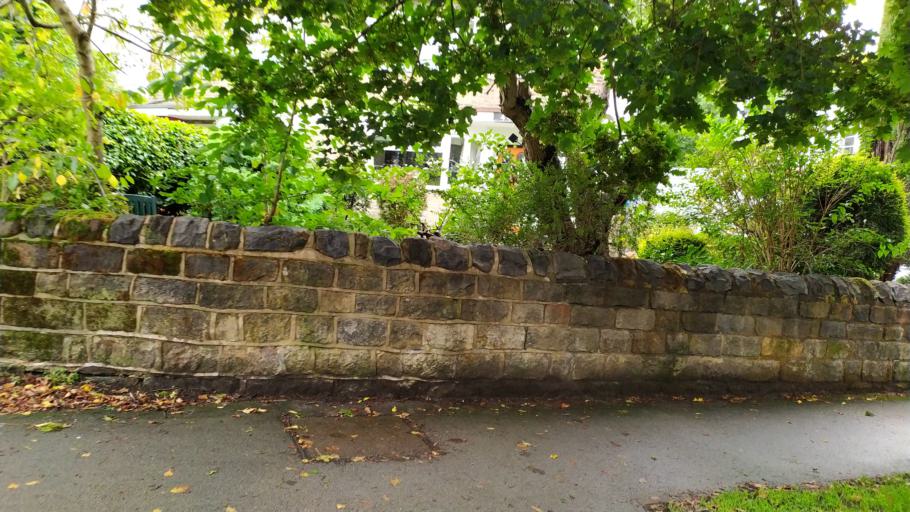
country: GB
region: England
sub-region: City and Borough of Leeds
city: Chapel Allerton
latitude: 53.8242
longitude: -1.5728
